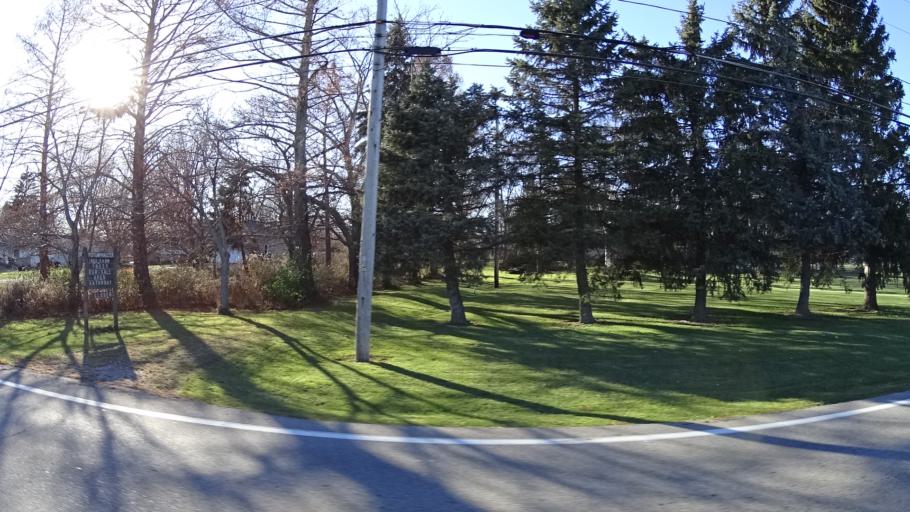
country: US
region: Ohio
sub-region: Lorain County
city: Elyria
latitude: 41.3634
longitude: -82.1447
